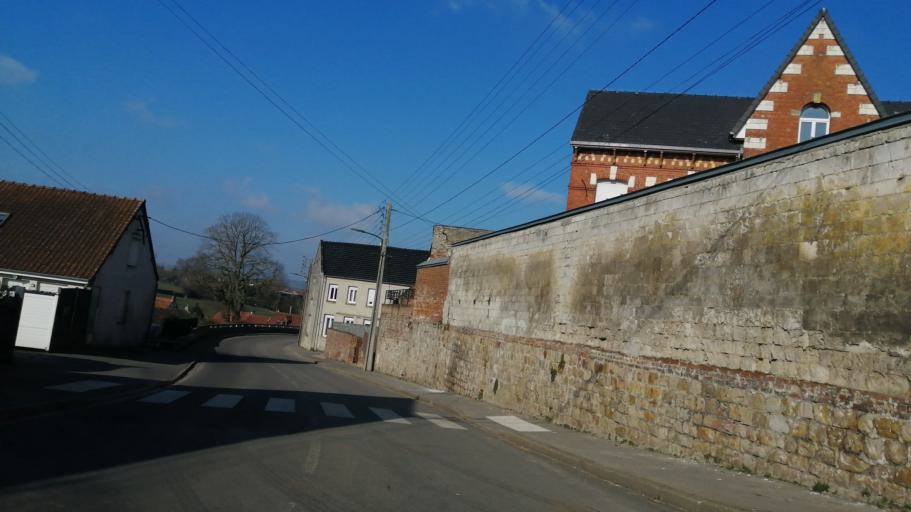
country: FR
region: Nord-Pas-de-Calais
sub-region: Departement du Pas-de-Calais
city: Ranchicourt
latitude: 50.4362
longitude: 2.5562
